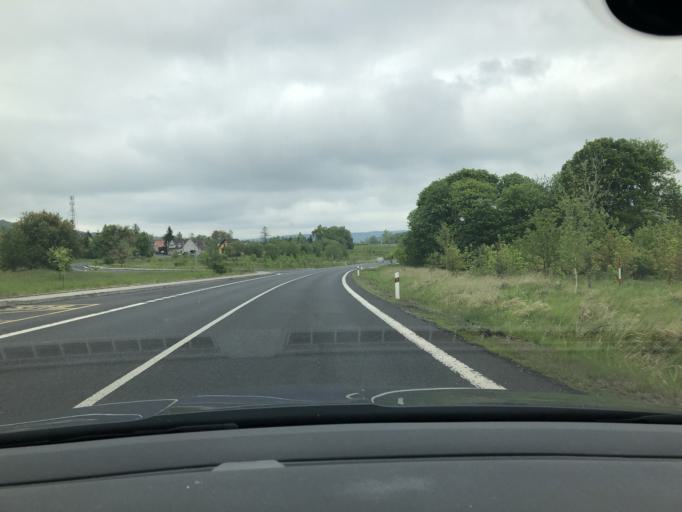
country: CZ
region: Ustecky
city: Libouchec
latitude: 50.7218
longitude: 14.0088
